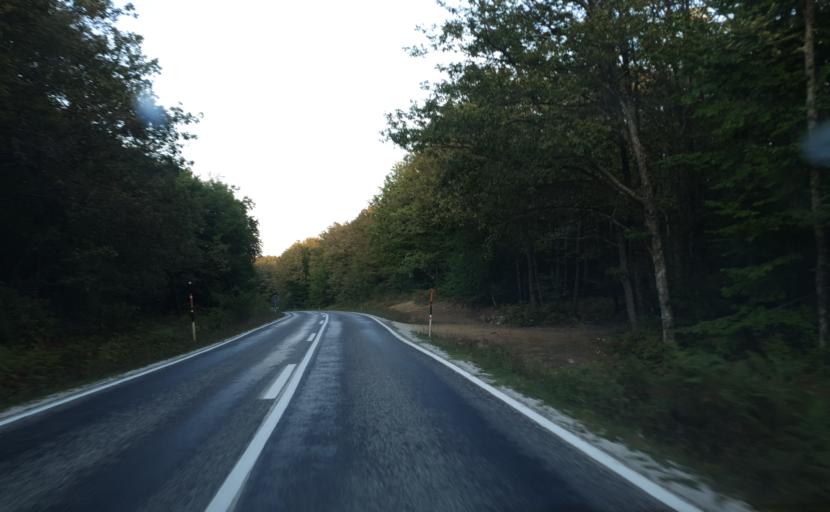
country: TR
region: Kirklareli
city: Igneada
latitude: 41.8744
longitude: 27.8150
